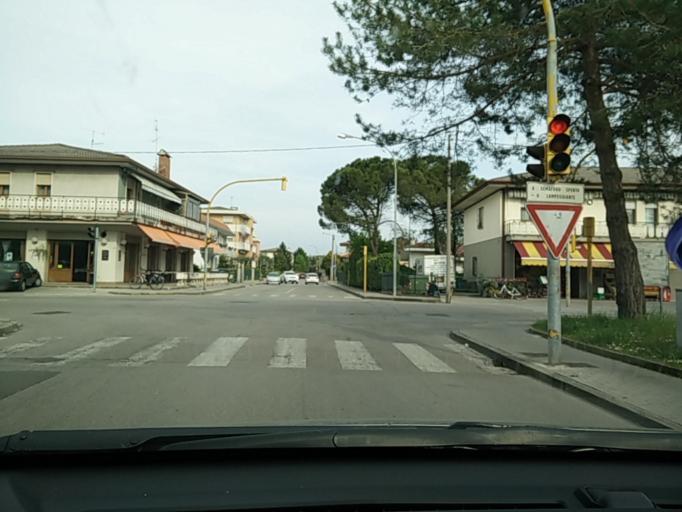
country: IT
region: Veneto
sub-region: Provincia di Venezia
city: San Dona di Piave
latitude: 45.6290
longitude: 12.5850
